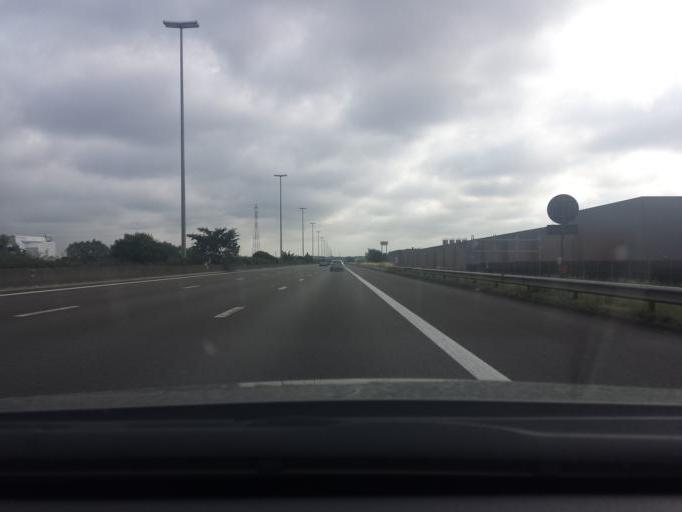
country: BE
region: Flanders
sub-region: Provincie West-Vlaanderen
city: Waregem
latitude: 50.8619
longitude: 3.4156
